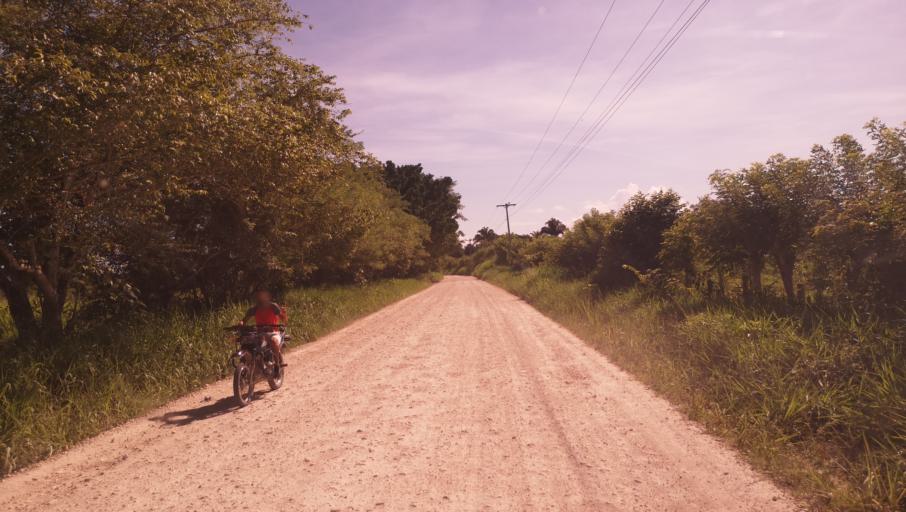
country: GT
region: Peten
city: Dolores
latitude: 16.7184
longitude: -89.3617
